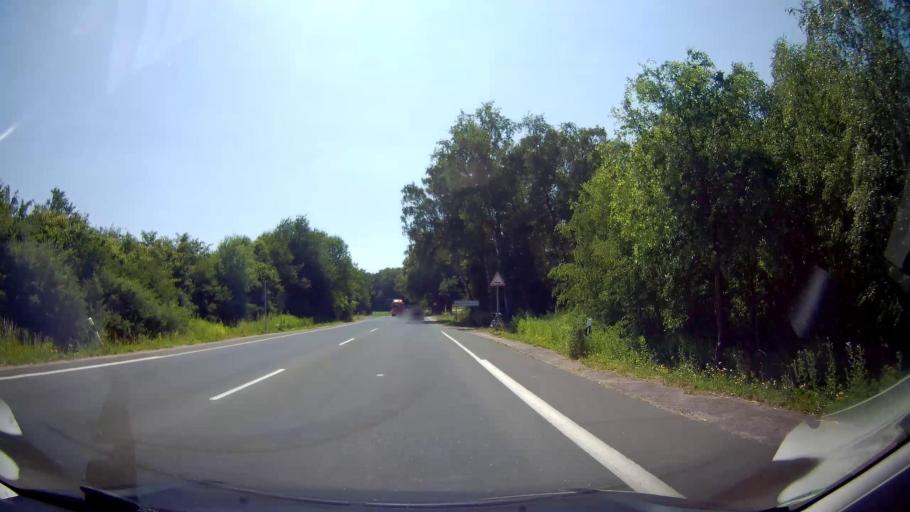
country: DE
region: North Rhine-Westphalia
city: Marl
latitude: 51.6535
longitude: 7.0380
